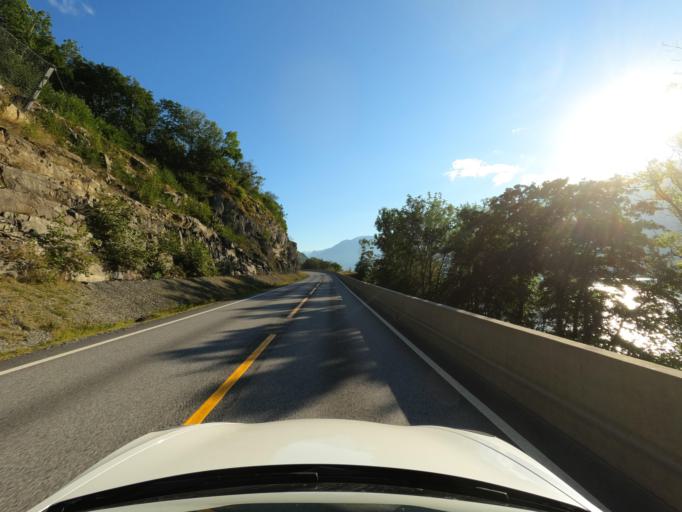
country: NO
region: Hordaland
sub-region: Ullensvang
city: Kinsarvik
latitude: 60.3036
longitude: 6.6431
